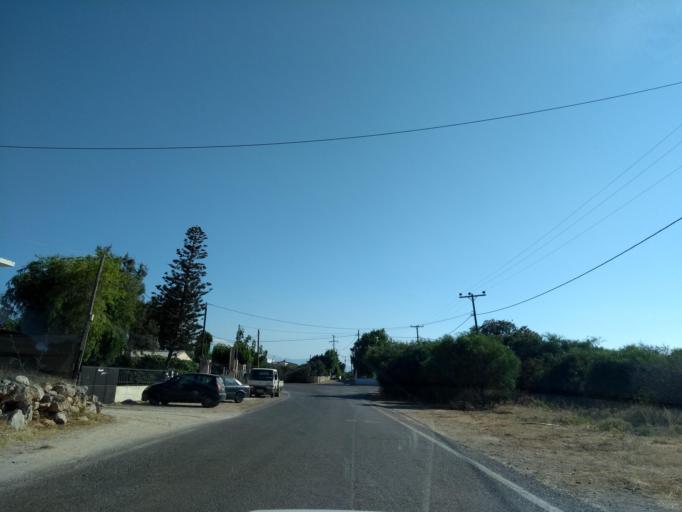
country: GR
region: Crete
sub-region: Nomos Chanias
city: Pithari
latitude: 35.5851
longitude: 24.0906
